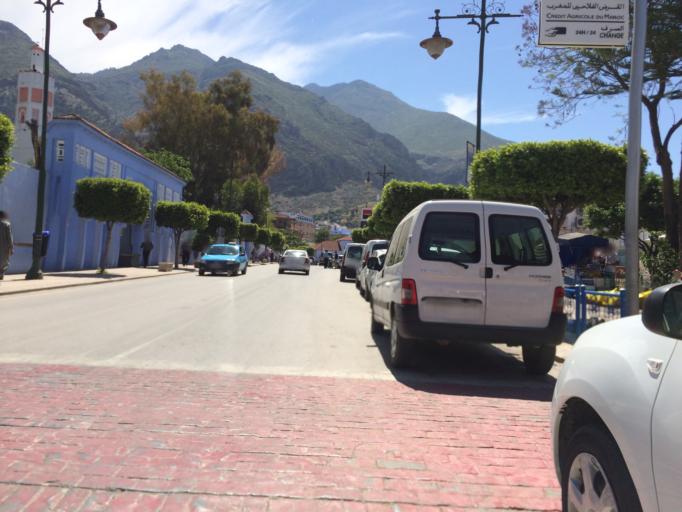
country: MA
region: Tanger-Tetouan
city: Chefchaouene
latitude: 35.1684
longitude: -5.2668
